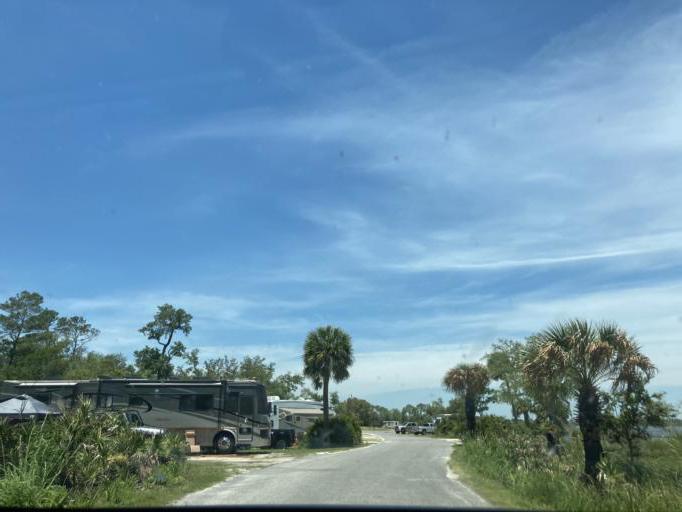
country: US
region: Florida
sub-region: Bay County
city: Lower Grand Lagoon
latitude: 30.1340
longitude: -85.7330
